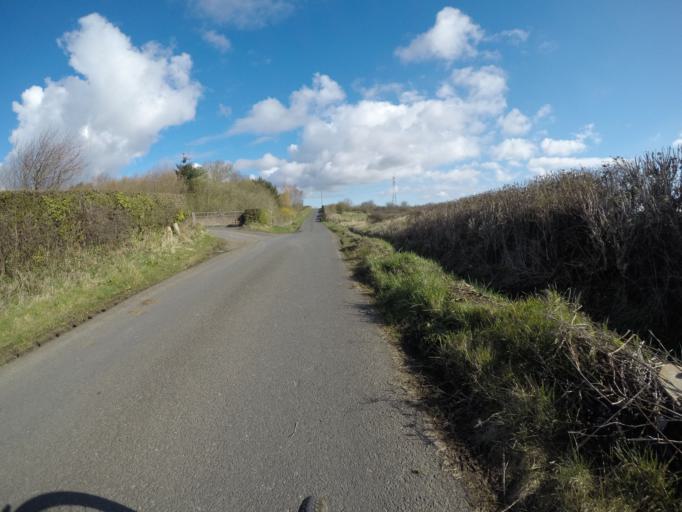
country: GB
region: Scotland
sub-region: North Ayrshire
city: Irvine
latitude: 55.6578
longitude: -4.6547
